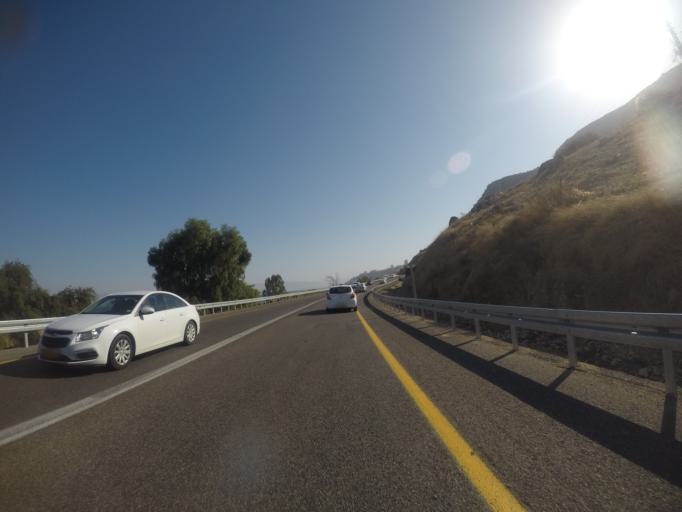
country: IL
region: Northern District
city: Tiberias
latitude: 32.8223
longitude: 35.5170
